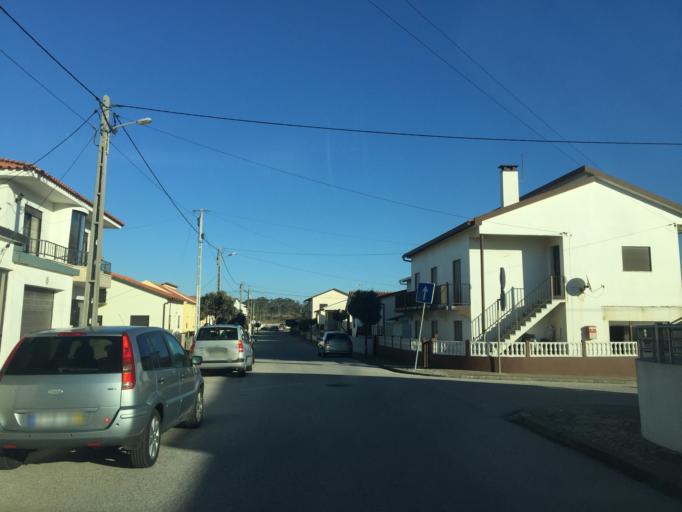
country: PT
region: Coimbra
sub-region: Figueira da Foz
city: Lavos
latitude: 40.0900
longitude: -8.8755
